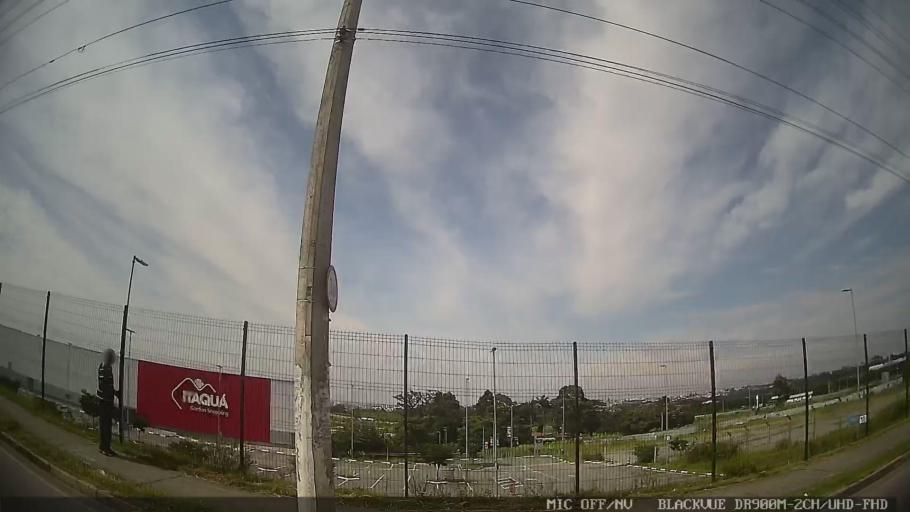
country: BR
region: Sao Paulo
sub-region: Itaquaquecetuba
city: Itaquaquecetuba
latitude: -23.4739
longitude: -46.3269
